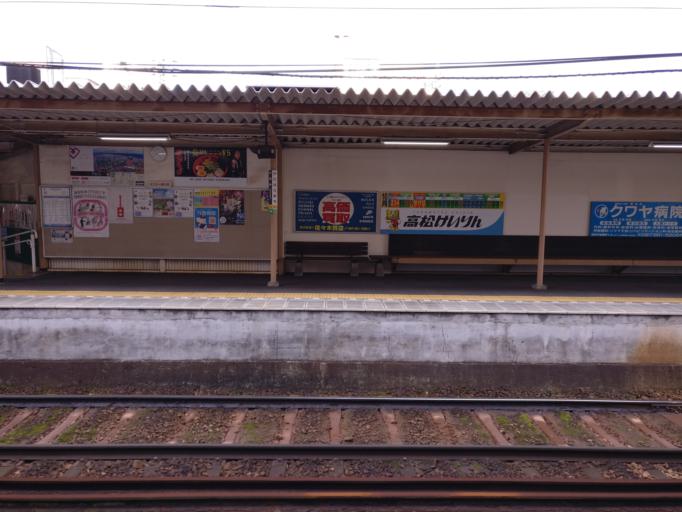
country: JP
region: Kagawa
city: Takamatsu-shi
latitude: 34.3459
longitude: 134.0542
